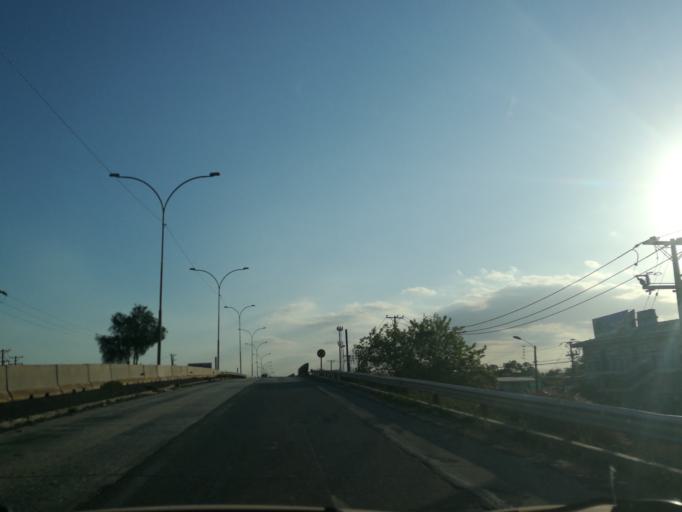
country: CL
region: O'Higgins
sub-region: Provincia de Cachapoal
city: Rancagua
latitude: -34.1783
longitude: -70.7324
